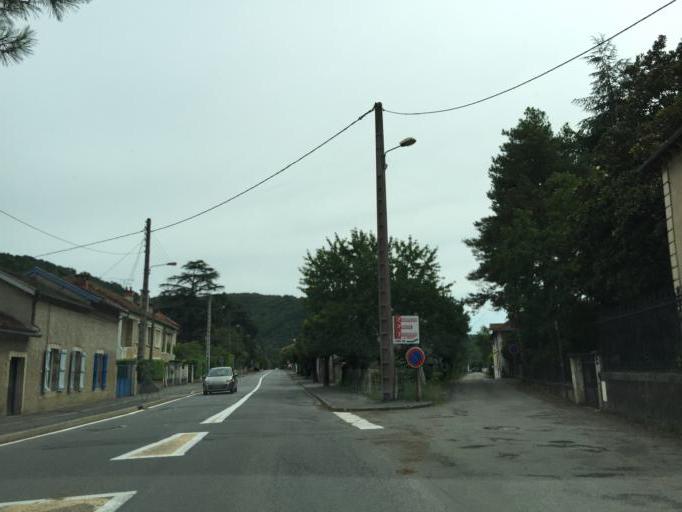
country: FR
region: Midi-Pyrenees
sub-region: Departement de l'Aveyron
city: Villefranche-de-Rouergue
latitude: 44.3426
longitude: 2.0321
